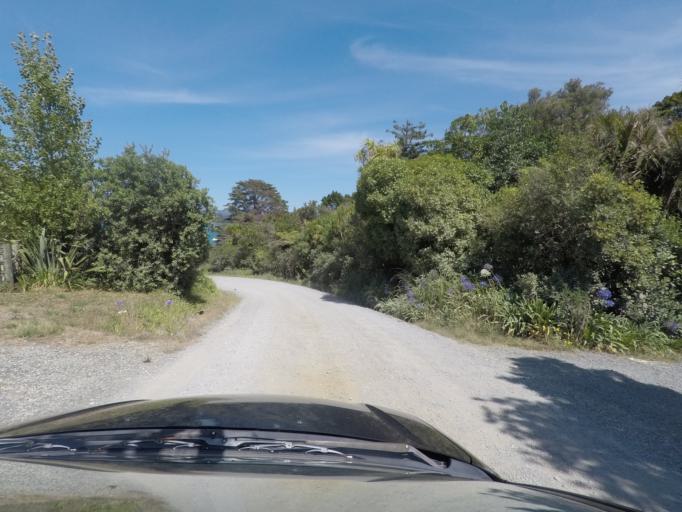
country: NZ
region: Auckland
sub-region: Auckland
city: Warkworth
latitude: -36.3161
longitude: 174.7871
